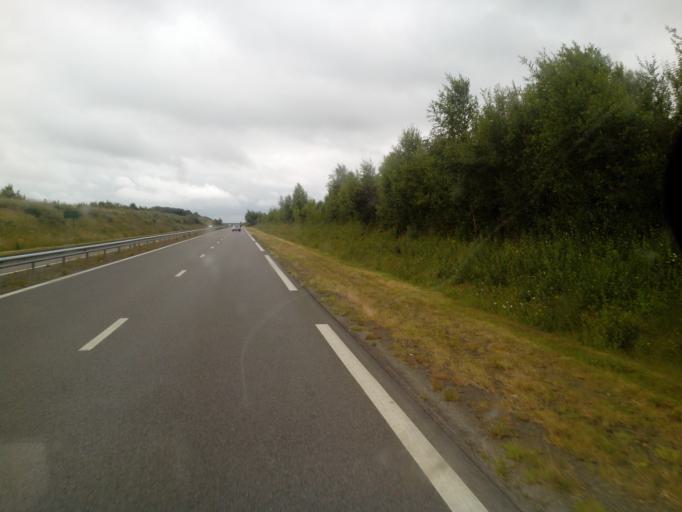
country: FR
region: Brittany
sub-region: Departement d'Ille-et-Vilaine
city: Betton
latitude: 48.1761
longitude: -1.6256
